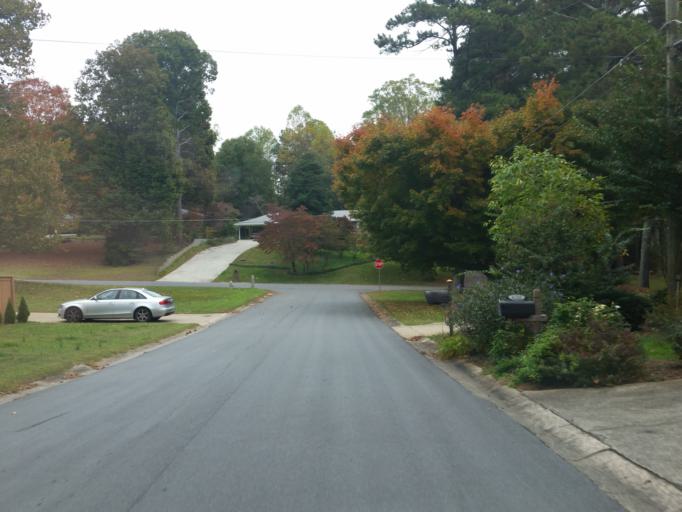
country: US
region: Georgia
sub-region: Cobb County
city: Marietta
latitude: 33.9655
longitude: -84.4839
